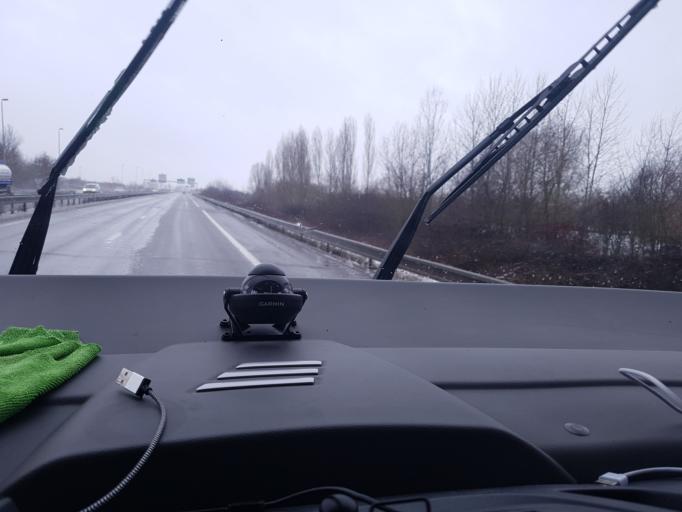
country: FR
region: Lorraine
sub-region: Departement de la Moselle
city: Peltre
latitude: 49.0969
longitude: 6.2341
